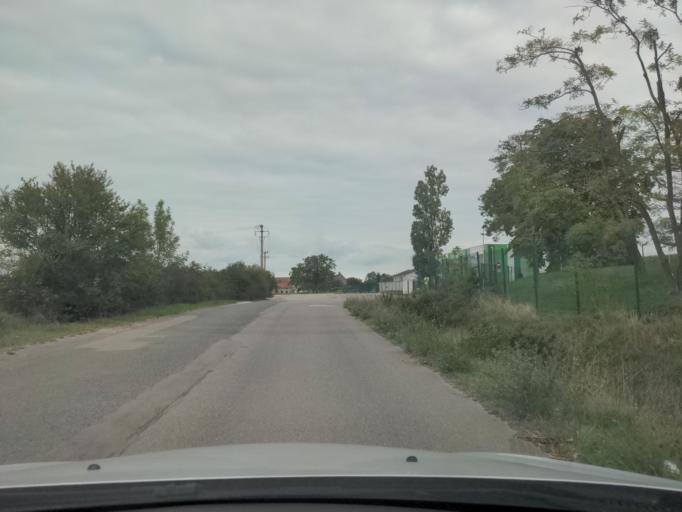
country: FR
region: Bourgogne
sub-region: Departement de la Cote-d'Or
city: Ahuy
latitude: 47.3637
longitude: 5.0377
